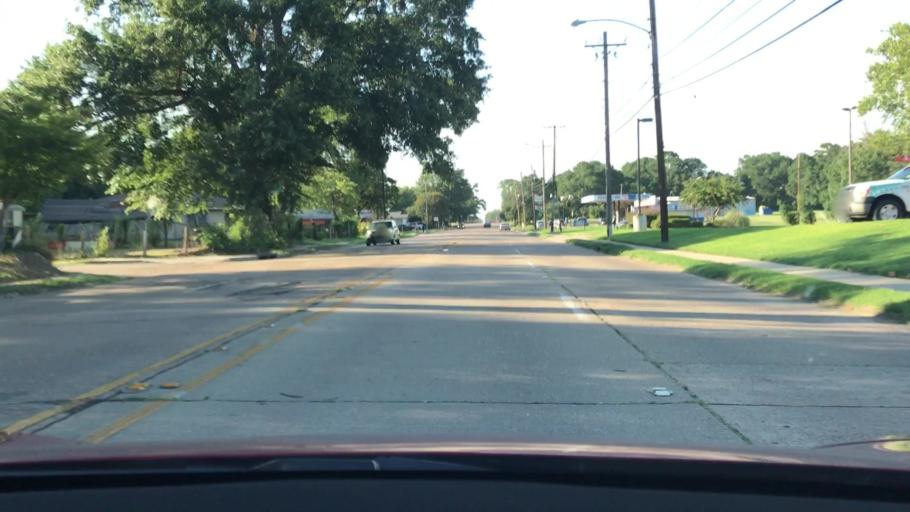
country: US
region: Louisiana
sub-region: Bossier Parish
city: Bossier City
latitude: 32.4352
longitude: -93.7459
